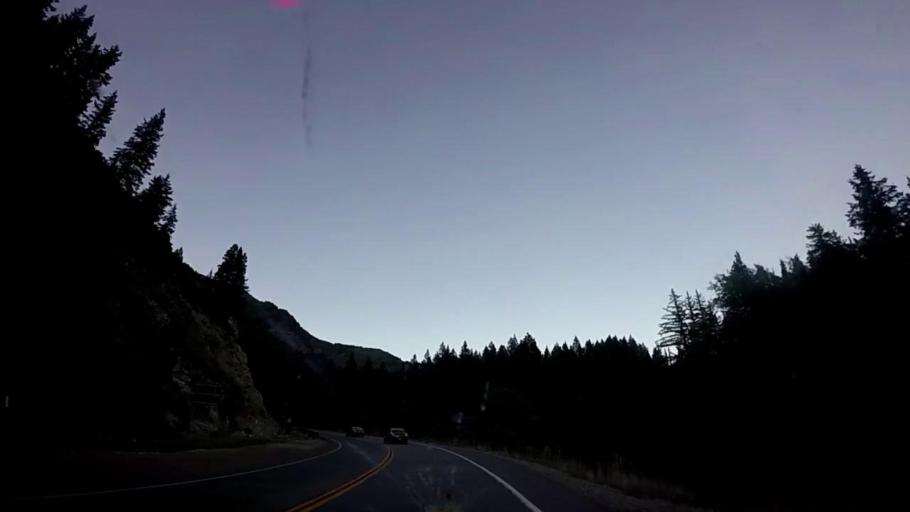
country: US
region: Utah
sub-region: Summit County
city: Summit Park
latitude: 40.6480
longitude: -111.6629
